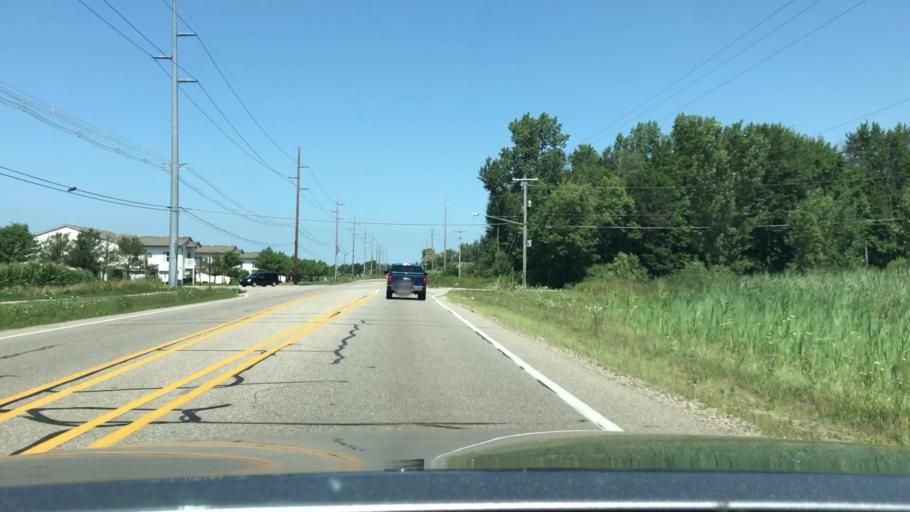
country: US
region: Michigan
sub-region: Ottawa County
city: Holland
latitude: 42.8333
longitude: -86.0786
